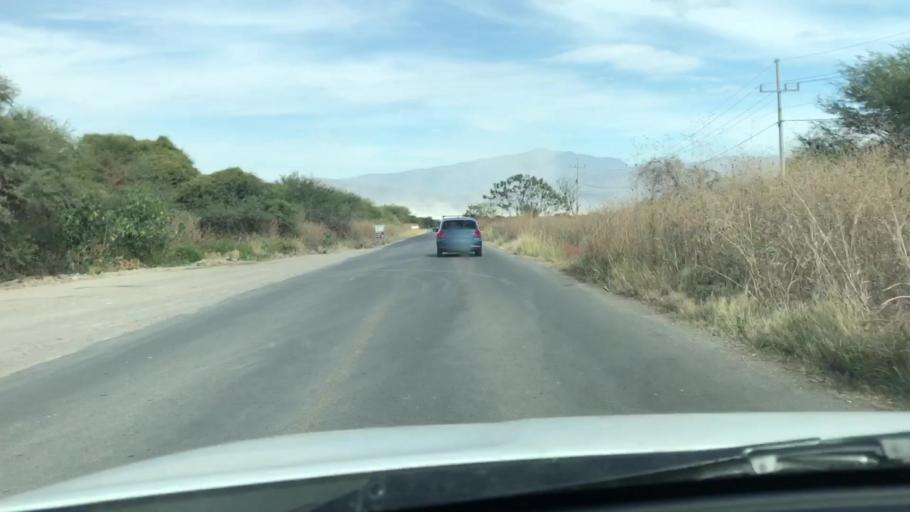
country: MX
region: Jalisco
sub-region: Zacoalco de Torres
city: Barranca de Otates (Barranca de Otatan)
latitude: 20.2780
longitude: -103.6263
